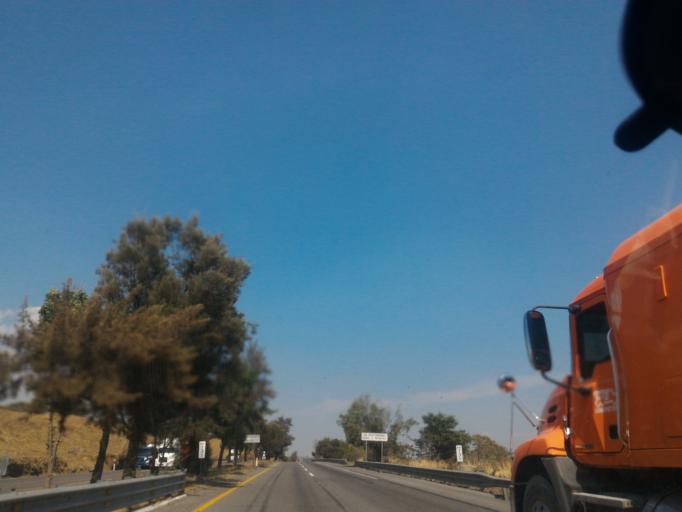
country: MX
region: Colima
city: Queseria
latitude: 19.3808
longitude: -103.5566
